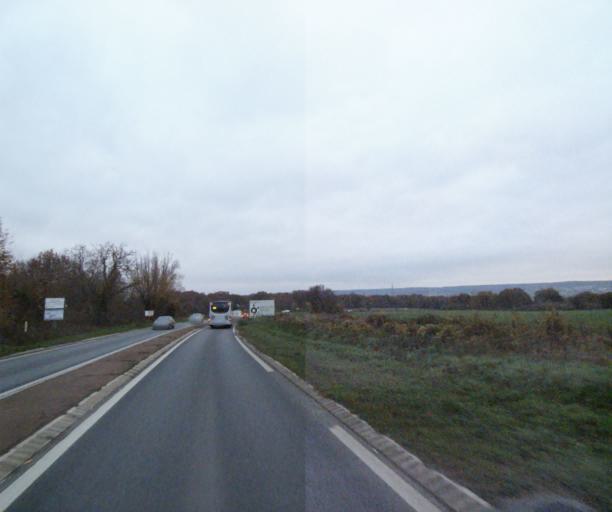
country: FR
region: Ile-de-France
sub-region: Departement des Yvelines
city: Vernouillet
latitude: 48.9567
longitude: 1.9802
